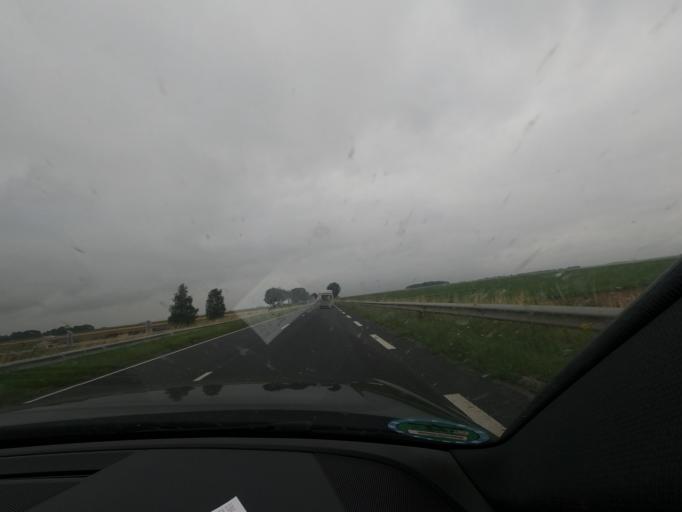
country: FR
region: Picardie
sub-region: Departement de la Somme
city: Rosieres-en-Santerre
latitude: 49.7404
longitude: 2.6869
